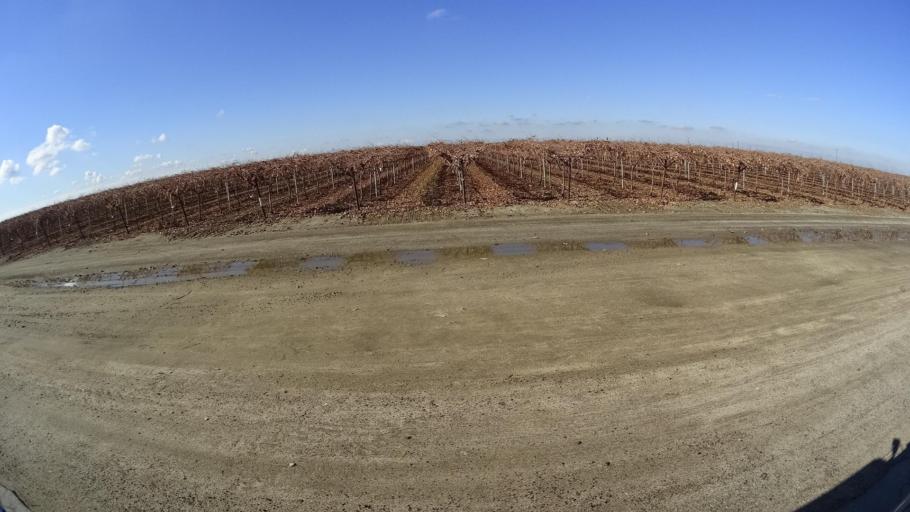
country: US
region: California
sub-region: Kern County
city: McFarland
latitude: 35.7156
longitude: -119.2586
